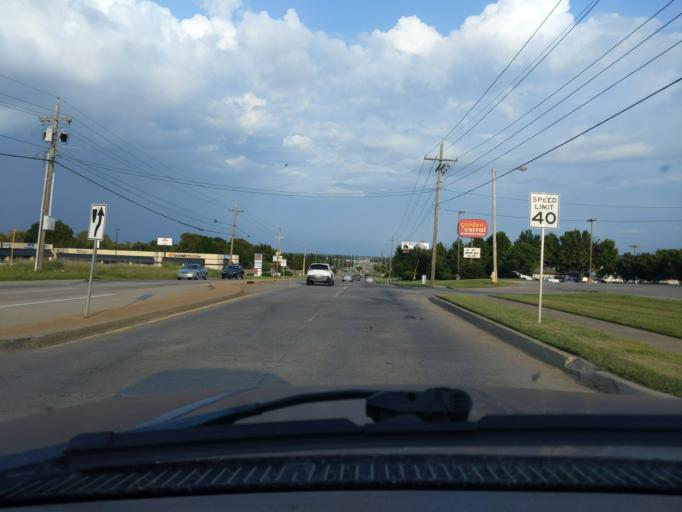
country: US
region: Oklahoma
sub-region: Tulsa County
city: Tulsa
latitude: 36.1334
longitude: -95.8854
